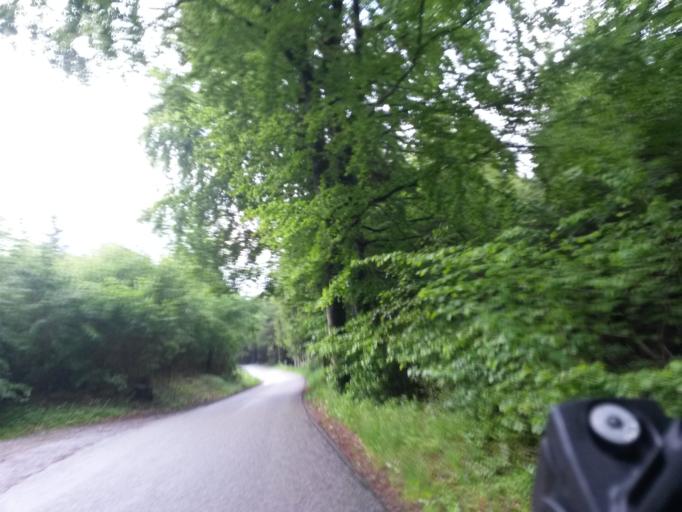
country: DE
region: Baden-Wuerttemberg
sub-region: Tuebingen Region
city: Eberhardzell
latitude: 47.9350
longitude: 9.8287
